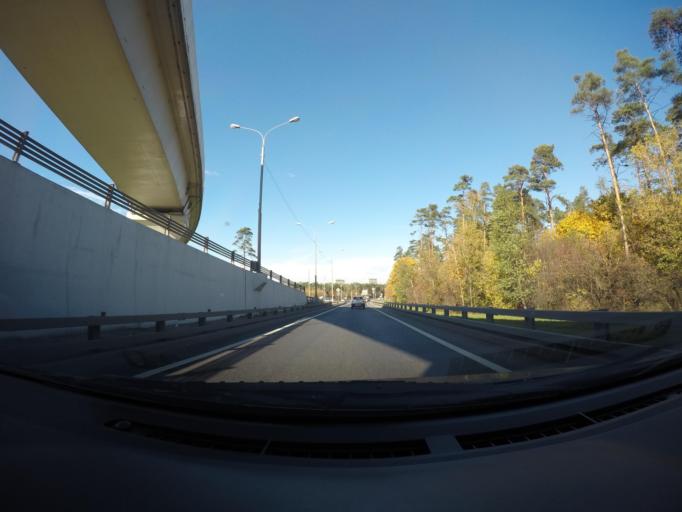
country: RU
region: Moscow
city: Zhulebino
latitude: 55.6885
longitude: 37.8319
